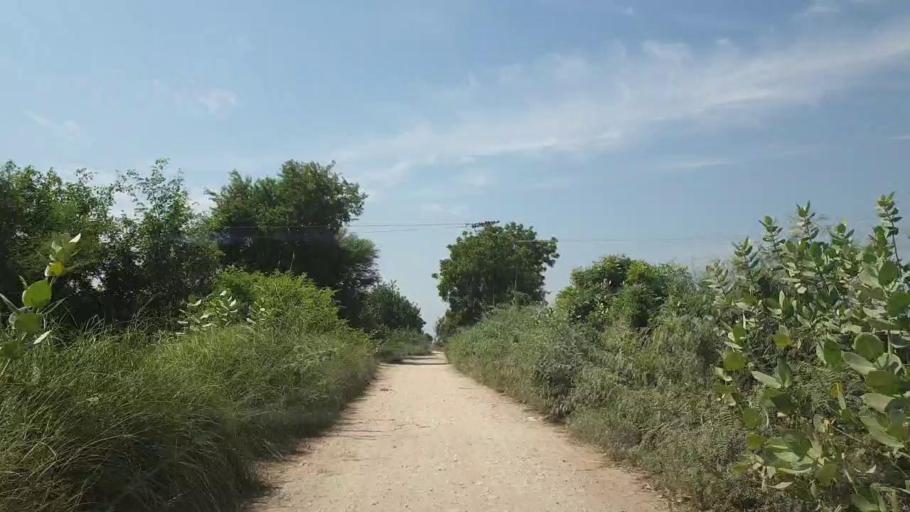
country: PK
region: Sindh
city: Tando Jam
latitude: 25.3991
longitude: 68.6146
